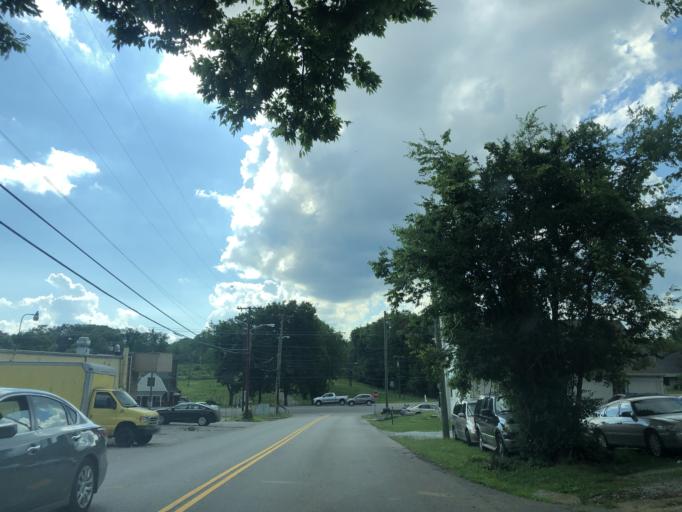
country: US
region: Tennessee
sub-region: Davidson County
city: Nashville
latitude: 36.2198
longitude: -86.7613
